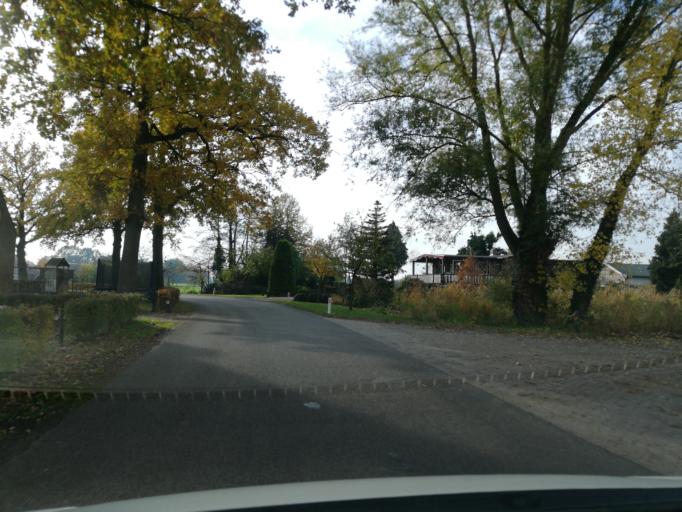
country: NL
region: Gelderland
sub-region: Gemeente Apeldoorn
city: Apeldoorn
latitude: 52.2451
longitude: 6.0292
